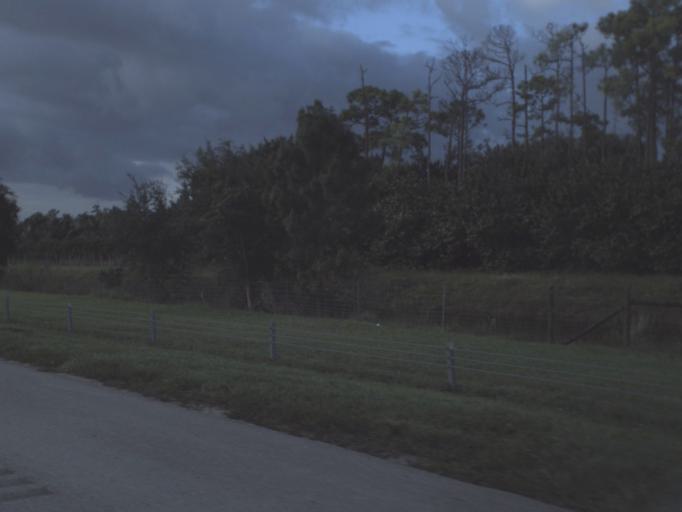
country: US
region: Florida
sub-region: Palm Beach County
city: Greenacres City
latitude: 26.6319
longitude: -80.1754
